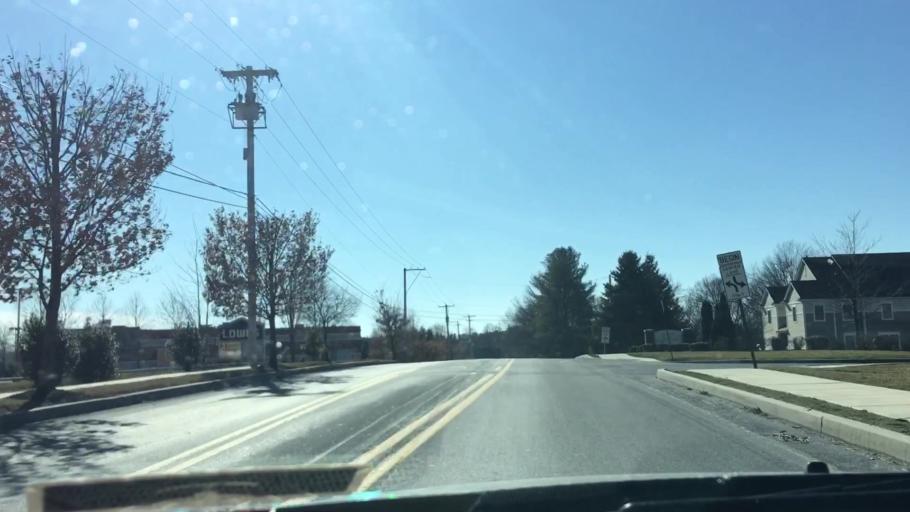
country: US
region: Pennsylvania
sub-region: Lancaster County
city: Lancaster
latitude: 40.0555
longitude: -76.2590
